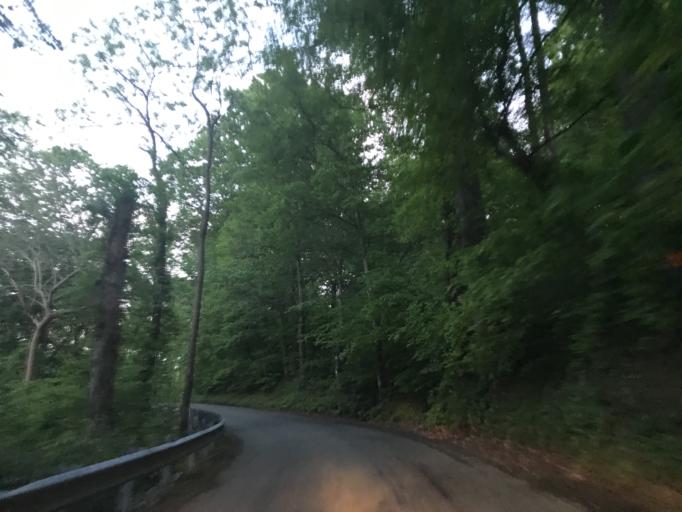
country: US
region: Maryland
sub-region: Harford County
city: Joppatowne
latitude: 39.4664
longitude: -76.3333
